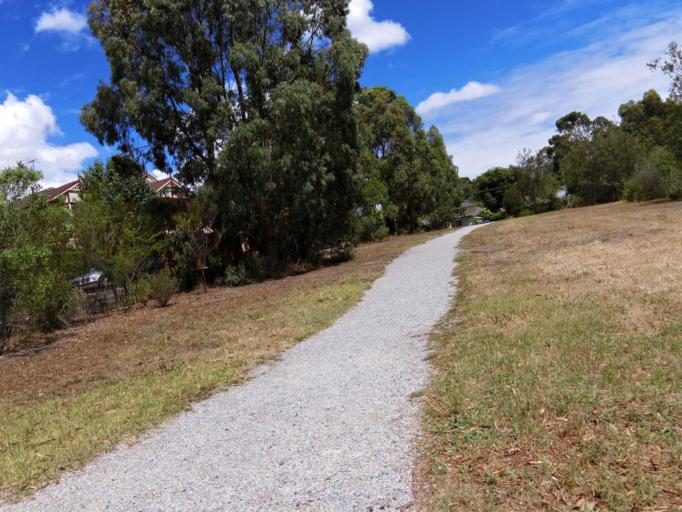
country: AU
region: Victoria
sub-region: Whitehorse
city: Blackburn South
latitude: -37.8423
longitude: 145.1481
